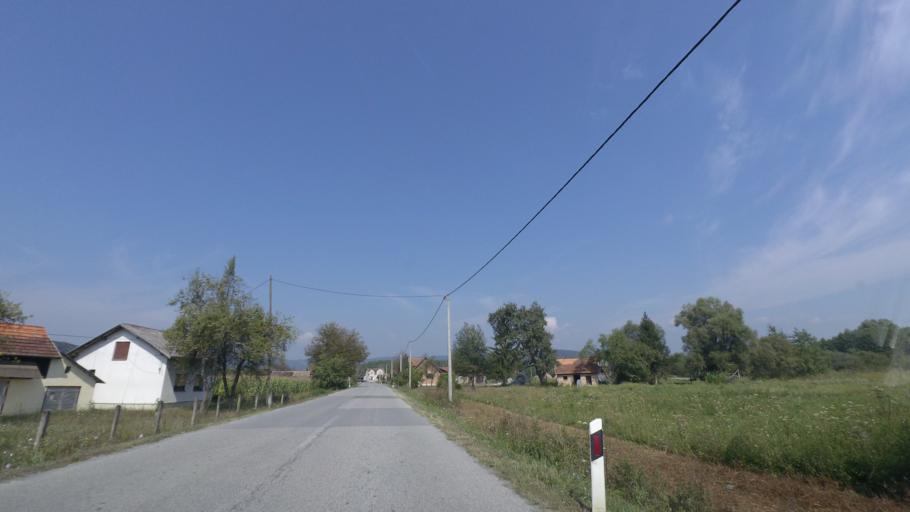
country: HR
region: Sisacko-Moslavacka
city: Dvor
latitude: 45.1131
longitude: 16.2768
